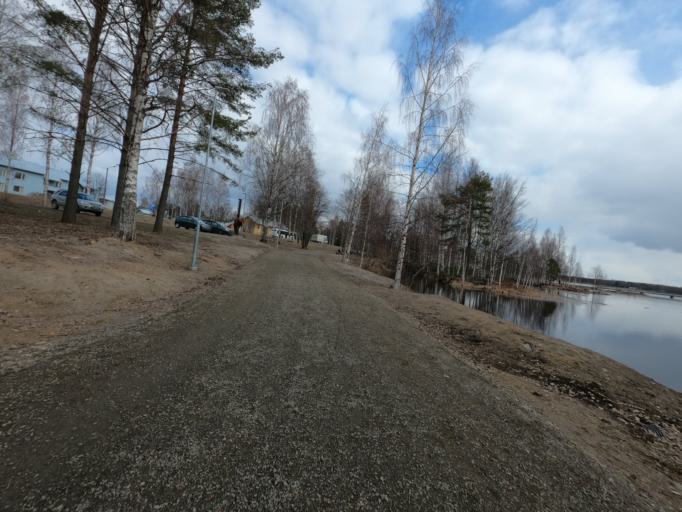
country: FI
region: North Karelia
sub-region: Joensuu
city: Joensuu
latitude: 62.6193
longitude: 29.8664
